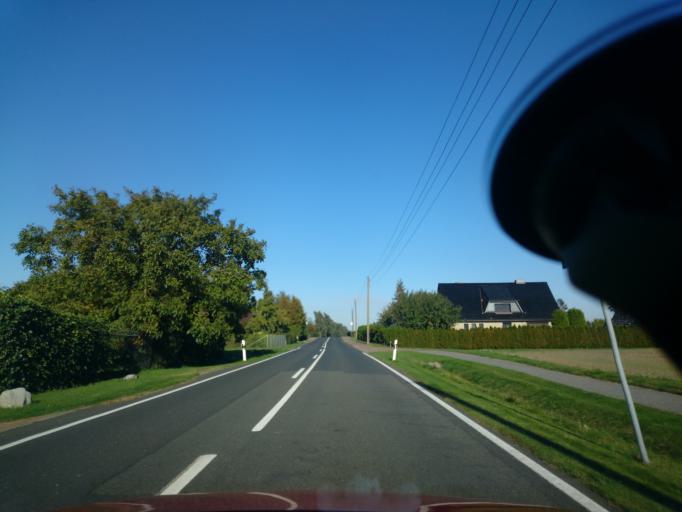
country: DE
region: Mecklenburg-Vorpommern
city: Saal
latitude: 54.3198
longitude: 12.5039
